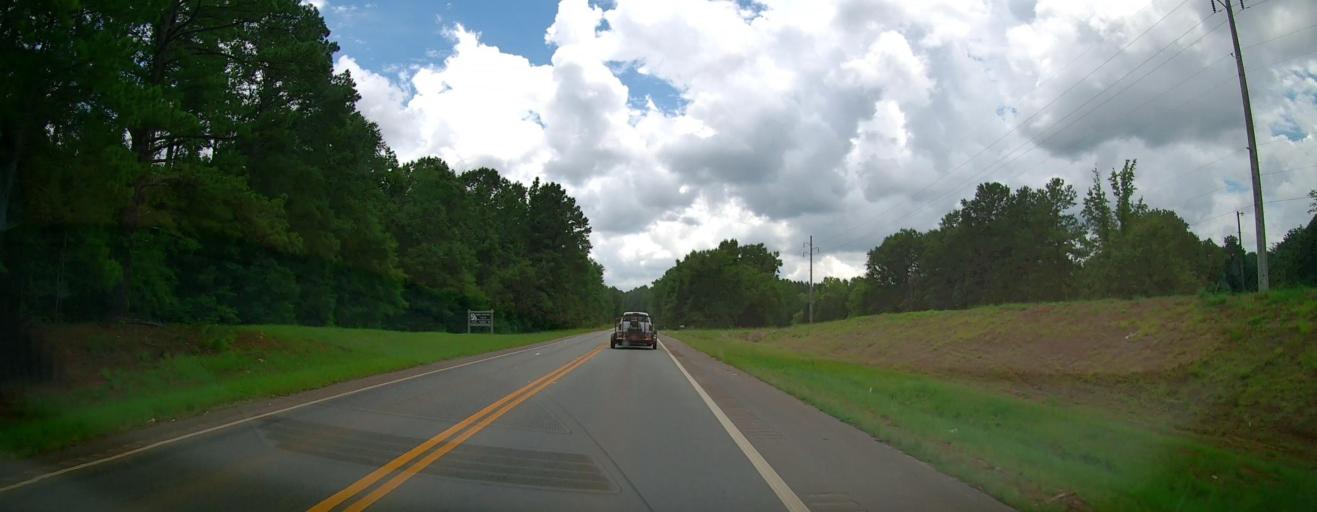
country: US
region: Georgia
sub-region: Pulaski County
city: Hawkinsville
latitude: 32.4116
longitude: -83.5706
